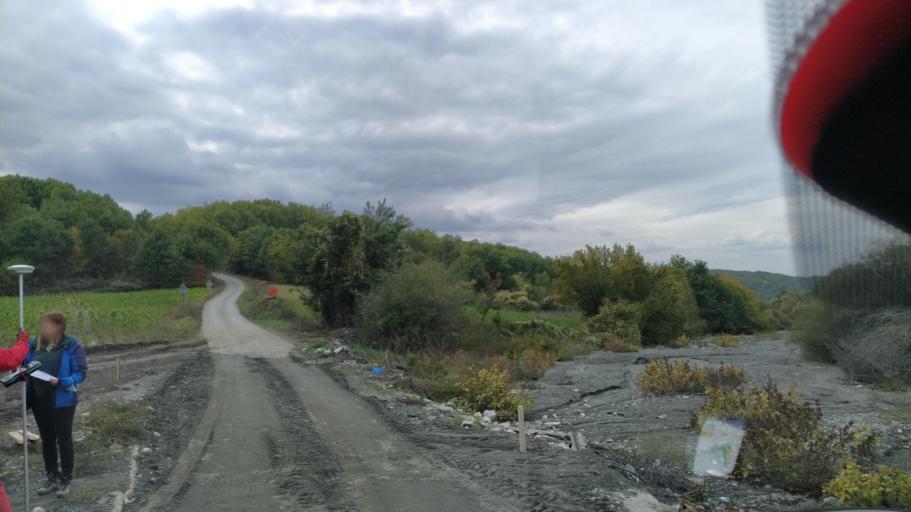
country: MK
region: Konce
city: Konce
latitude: 41.5076
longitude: 22.4641
